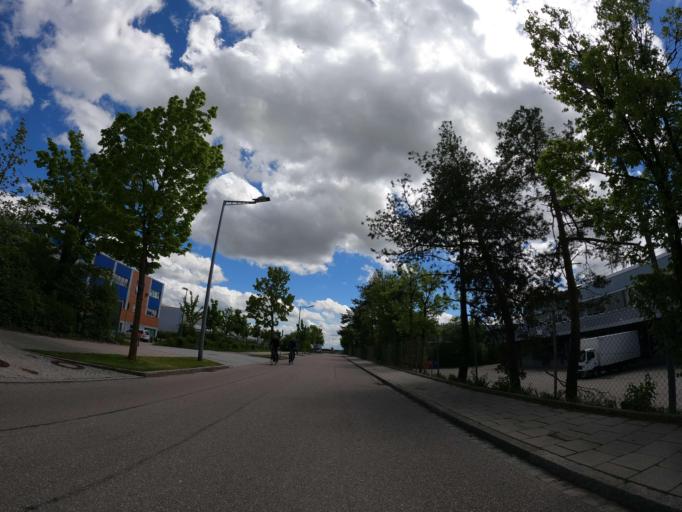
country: DE
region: Bavaria
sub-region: Upper Bavaria
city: Kirchheim bei Muenchen
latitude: 48.1560
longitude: 11.7597
